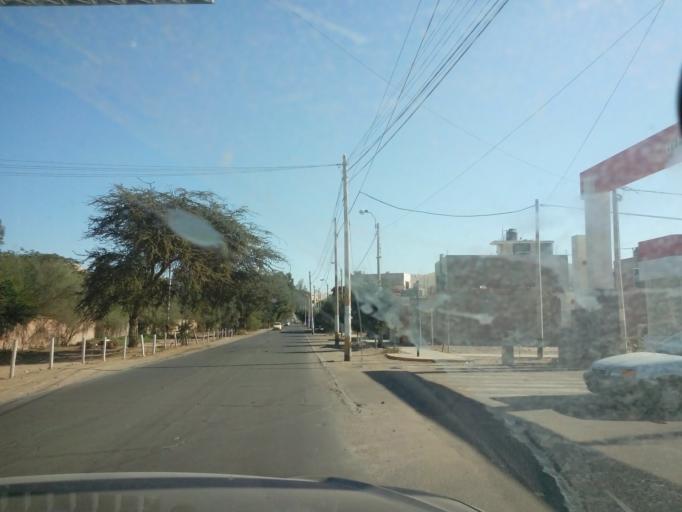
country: PE
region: Ica
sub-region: Provincia de Ica
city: Ica
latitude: -14.0812
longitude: -75.7496
